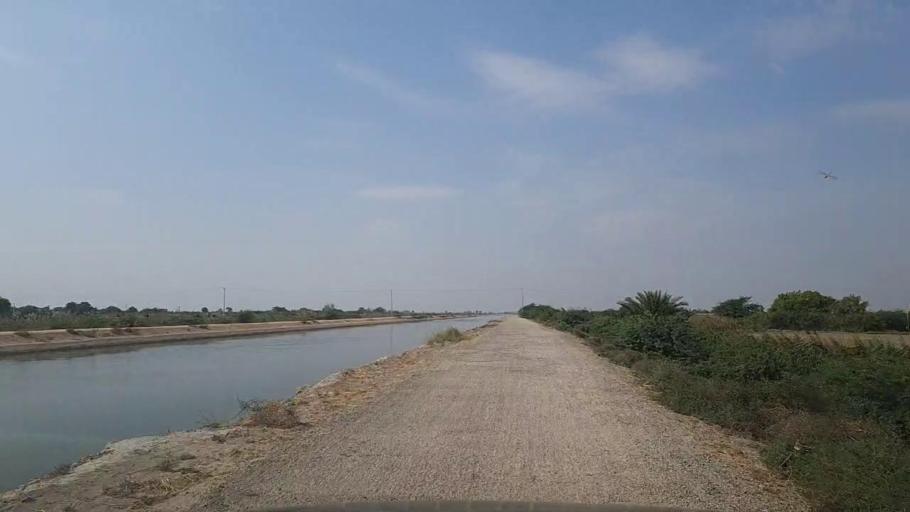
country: PK
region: Sindh
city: Thatta
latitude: 24.7525
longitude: 67.7678
